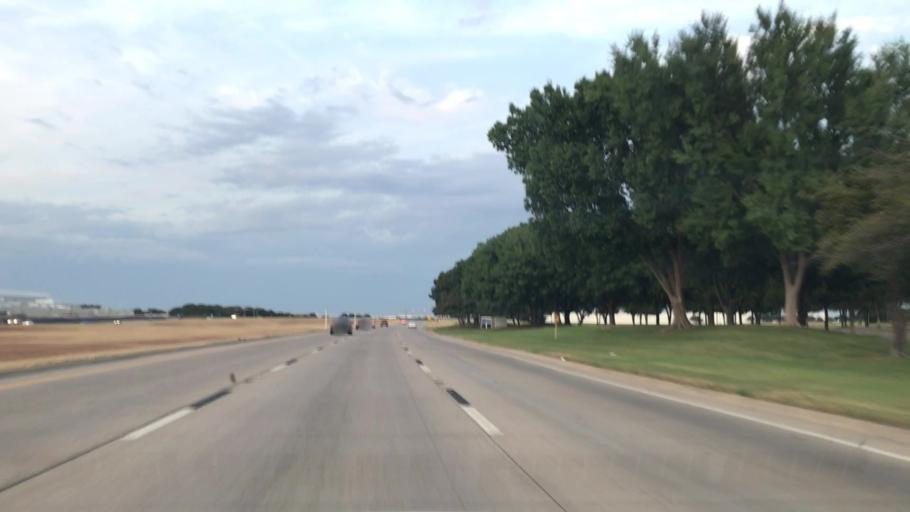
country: US
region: Texas
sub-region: Denton County
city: Roanoke
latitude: 32.9814
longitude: -97.2575
